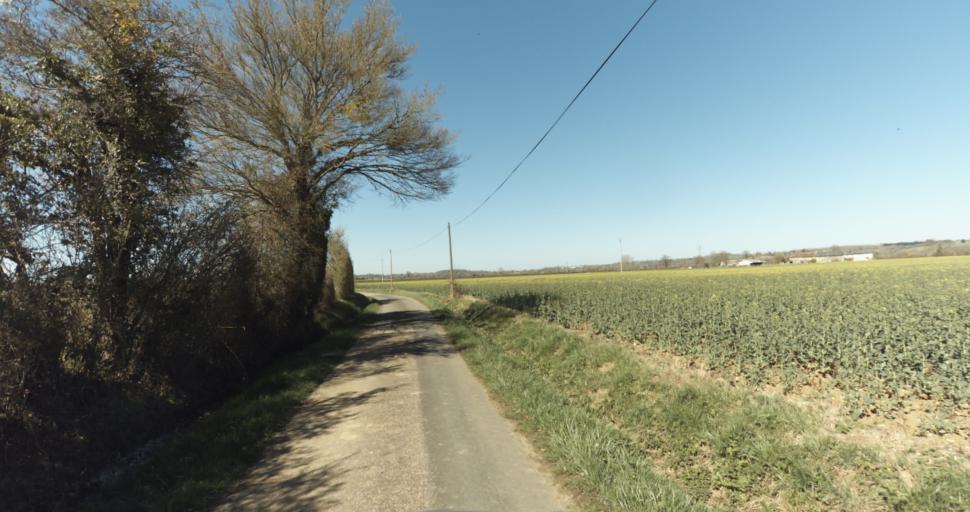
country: FR
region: Lower Normandy
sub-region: Departement du Calvados
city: Saint-Pierre-sur-Dives
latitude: 49.0324
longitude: 0.0104
